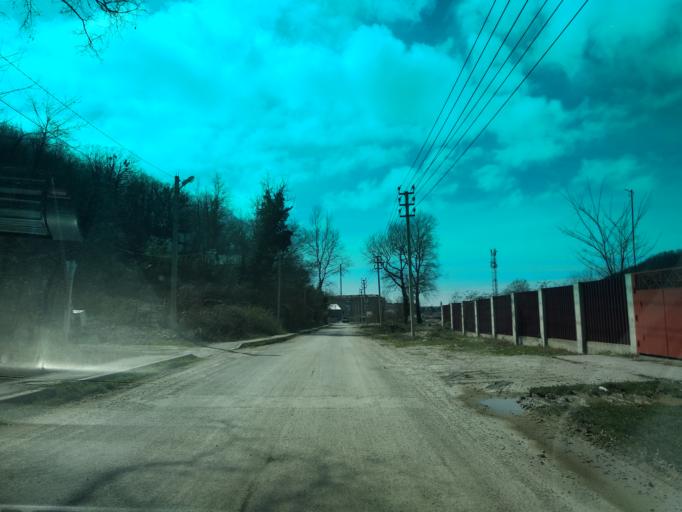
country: RU
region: Krasnodarskiy
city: Shepsi
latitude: 44.0470
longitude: 39.1574
